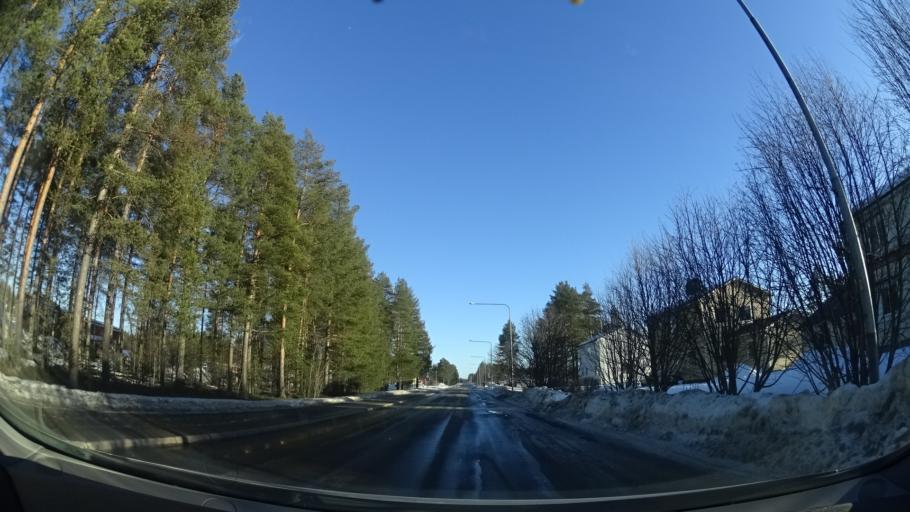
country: SE
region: Vaesterbotten
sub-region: Skelleftea Kommun
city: Langsele
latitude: 65.0575
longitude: 20.0460
